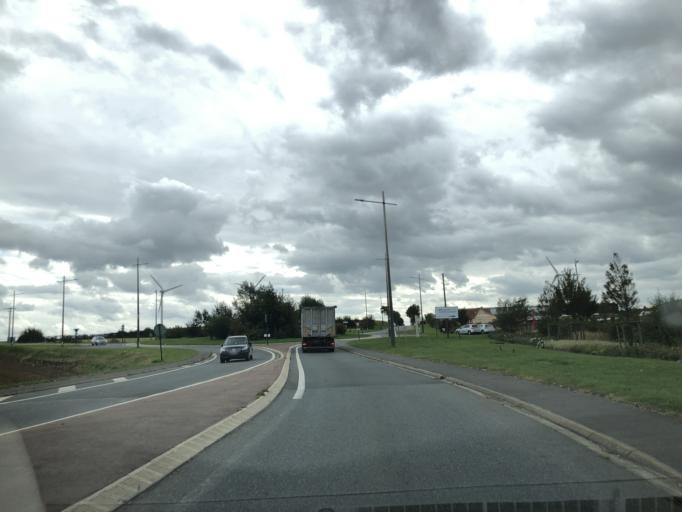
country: FR
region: Nord-Pas-de-Calais
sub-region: Departement du Pas-de-Calais
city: Fruges
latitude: 50.5008
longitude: 2.1298
